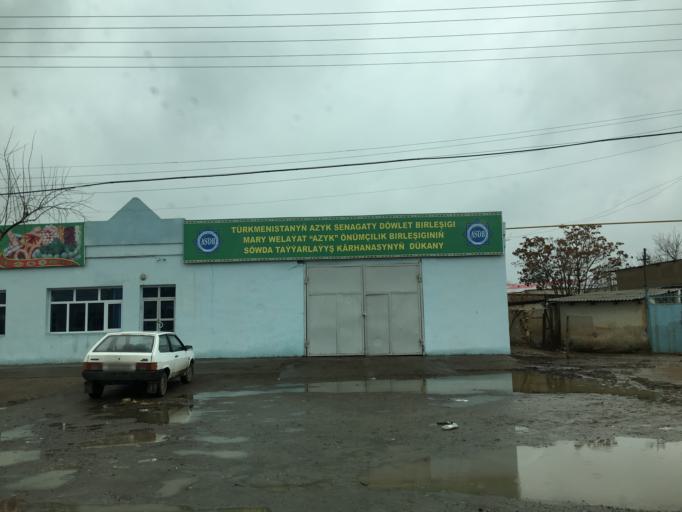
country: TM
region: Mary
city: Yoloeten
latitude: 37.3054
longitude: 62.3554
